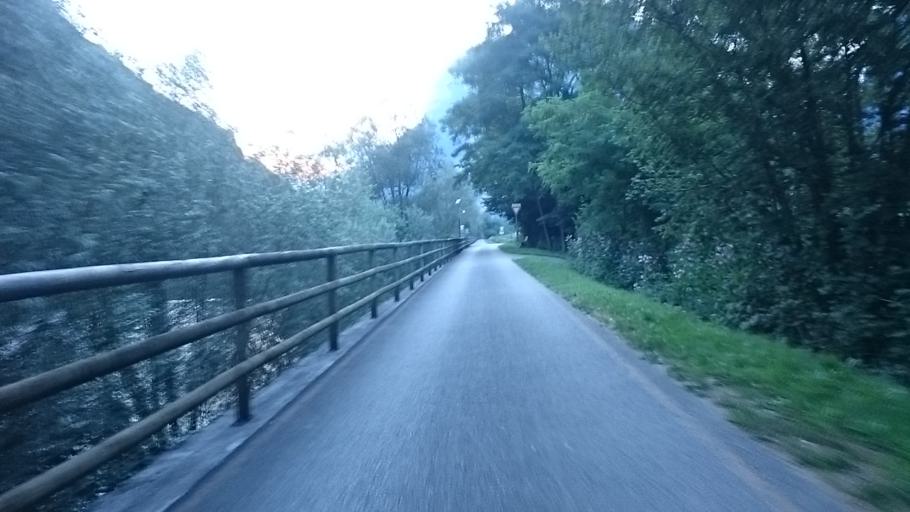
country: IT
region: Trentino-Alto Adige
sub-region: Provincia di Trento
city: Grigno
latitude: 46.0039
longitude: 11.6455
